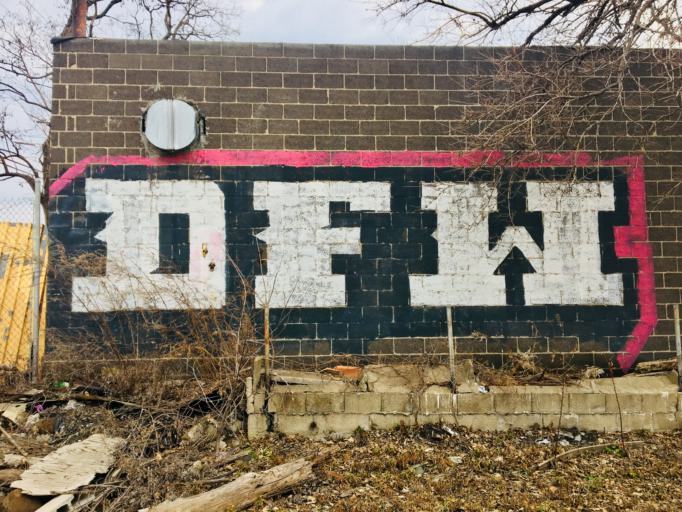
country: US
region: Michigan
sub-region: Wayne County
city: River Rouge
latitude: 42.2963
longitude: -83.1288
